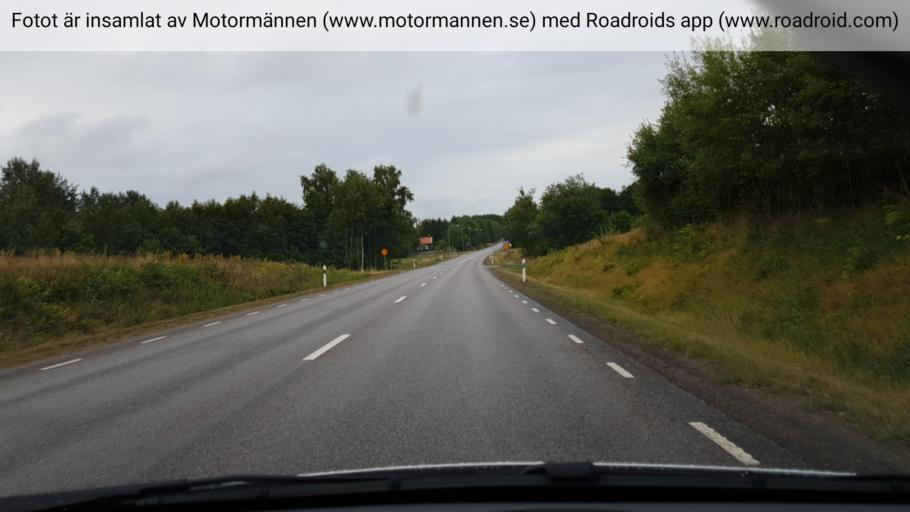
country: SE
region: Vaestra Goetaland
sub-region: Karlsborgs Kommun
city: Molltorp
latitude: 58.4643
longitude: 14.2918
